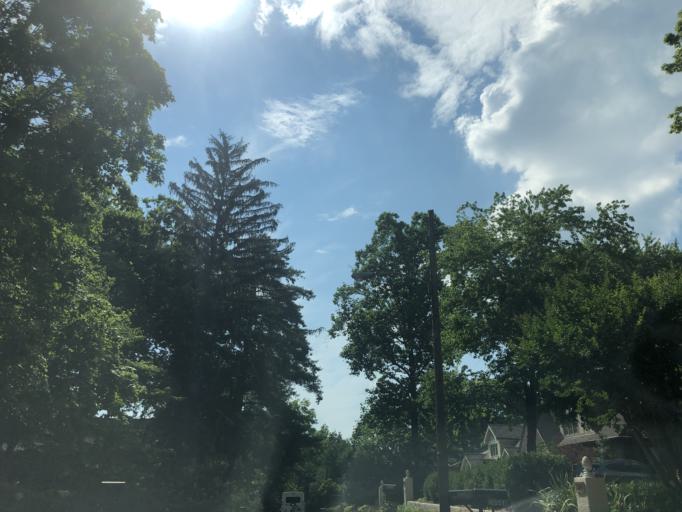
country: US
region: Tennessee
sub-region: Davidson County
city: Belle Meade
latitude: 36.1251
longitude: -86.8239
